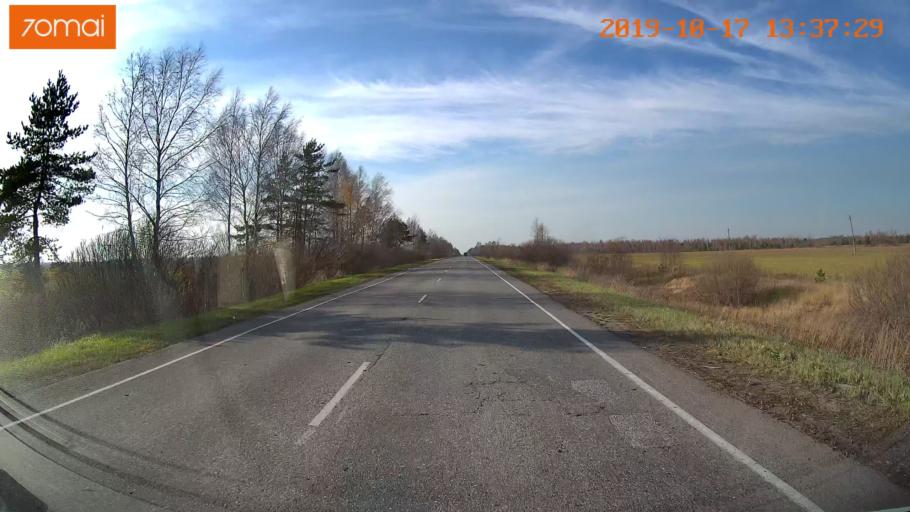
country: RU
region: Rjazan
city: Tuma
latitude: 55.1417
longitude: 40.6380
